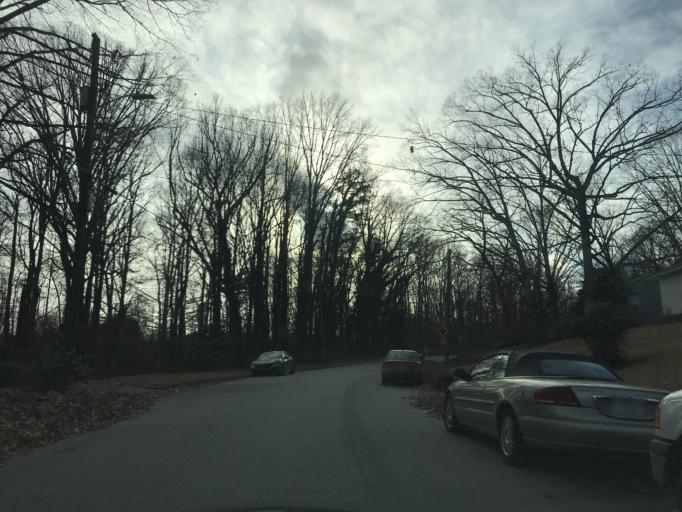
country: US
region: North Carolina
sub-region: Wake County
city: Raleigh
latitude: 35.7993
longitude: -78.6123
